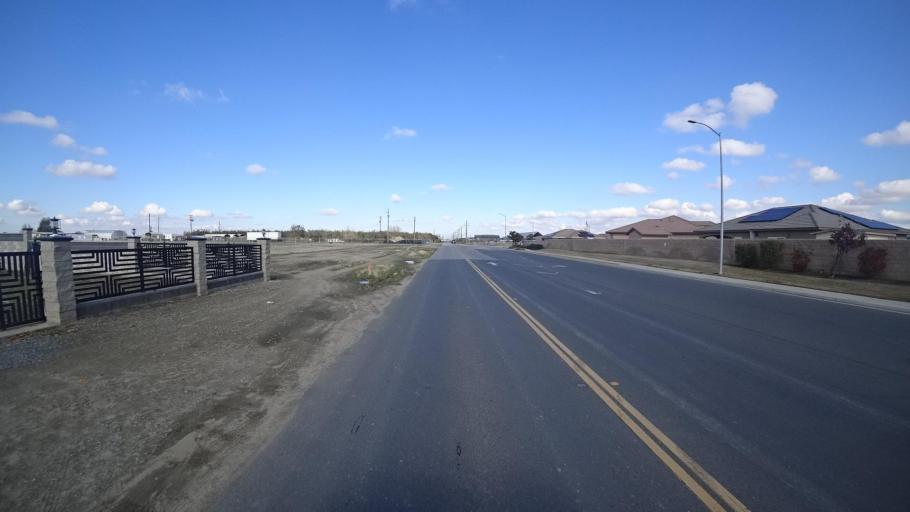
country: US
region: California
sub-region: Kern County
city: McFarland
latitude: 35.6842
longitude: -119.2409
